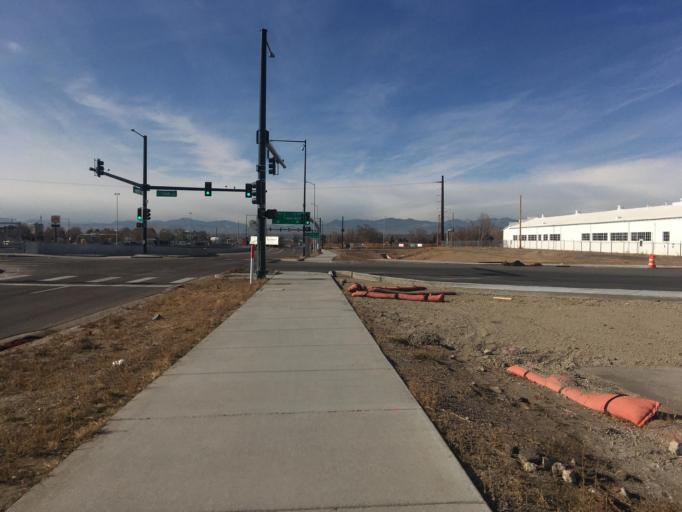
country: US
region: Colorado
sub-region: Adams County
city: Commerce City
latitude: 39.7809
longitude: -104.9472
